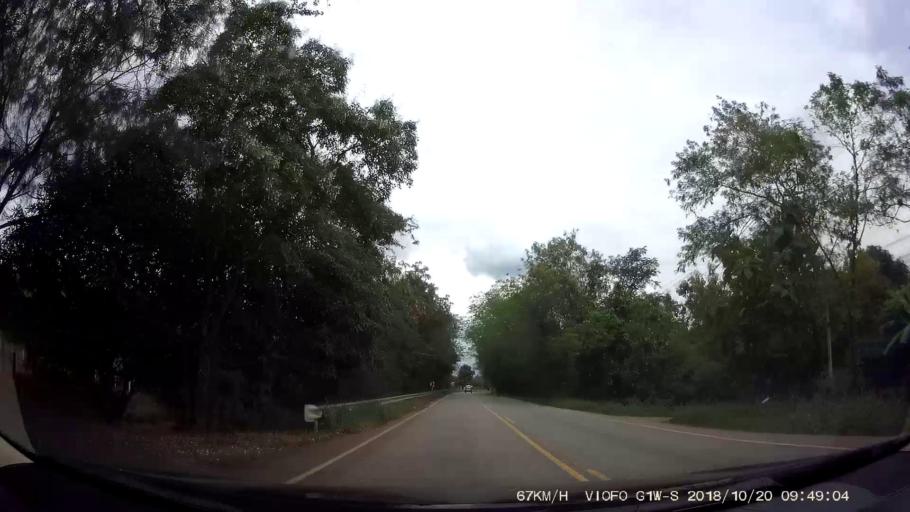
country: TH
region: Chaiyaphum
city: Khon San
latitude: 16.5161
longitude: 101.9073
